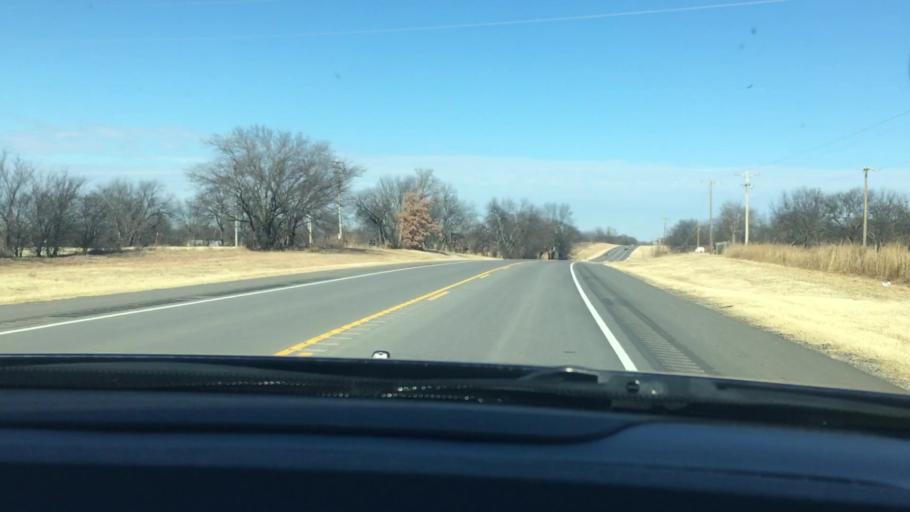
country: US
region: Oklahoma
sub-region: Murray County
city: Davis
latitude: 34.5491
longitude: -97.1322
